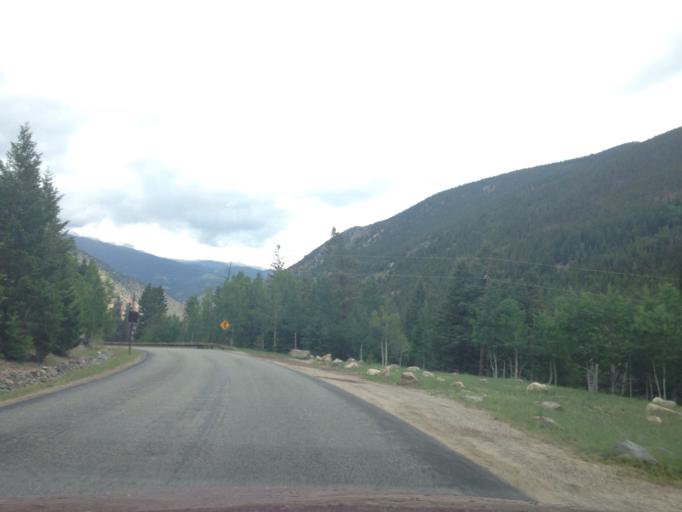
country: US
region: Colorado
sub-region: Clear Creek County
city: Georgetown
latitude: 39.6991
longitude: -105.6949
